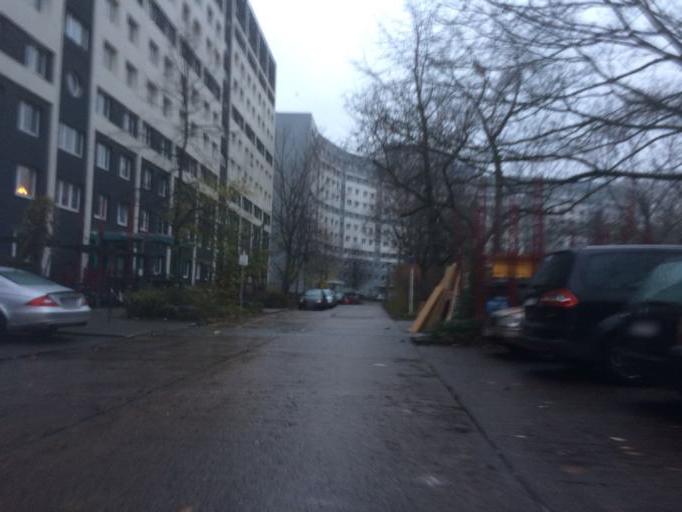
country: DE
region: Berlin
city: Berlin
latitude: 52.5132
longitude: 13.4304
